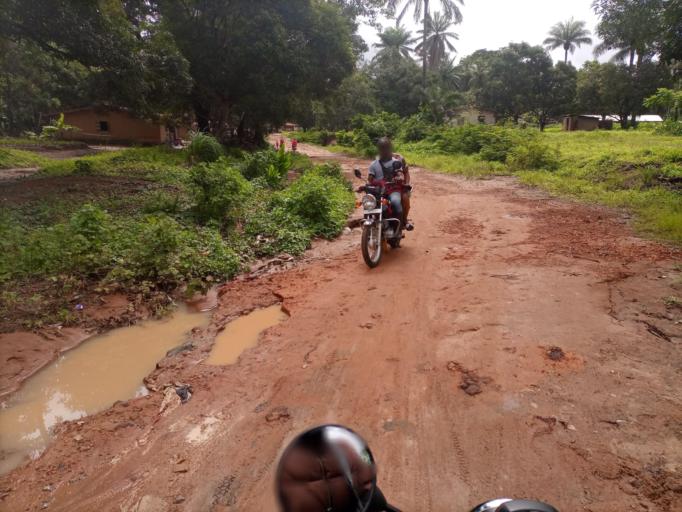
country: SL
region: Northern Province
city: Sawkta
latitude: 8.6353
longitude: -13.1984
